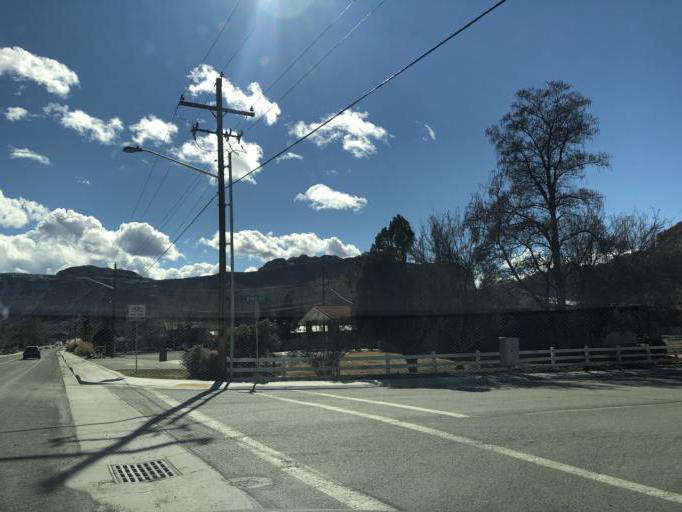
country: US
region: Utah
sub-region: Grand County
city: Moab
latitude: 38.5849
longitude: -109.5611
